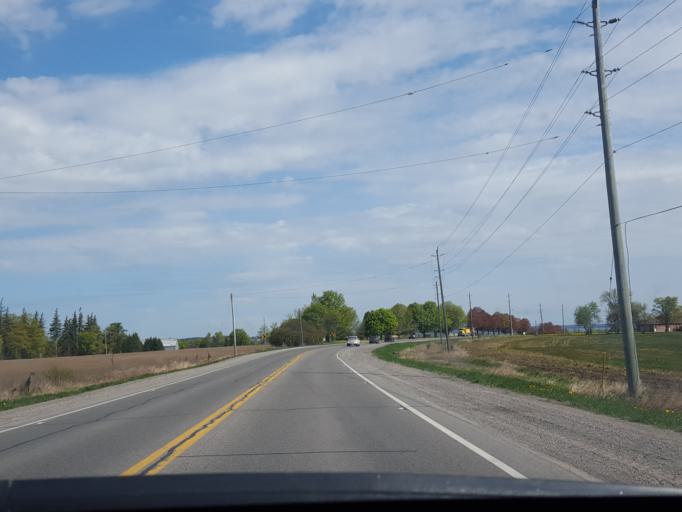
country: CA
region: Ontario
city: Uxbridge
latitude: 44.1153
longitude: -78.9209
